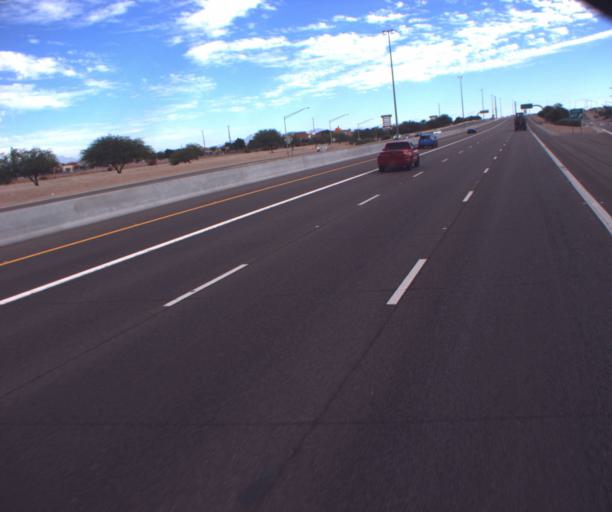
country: US
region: Arizona
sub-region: Maricopa County
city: Chandler
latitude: 33.2871
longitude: -111.8461
